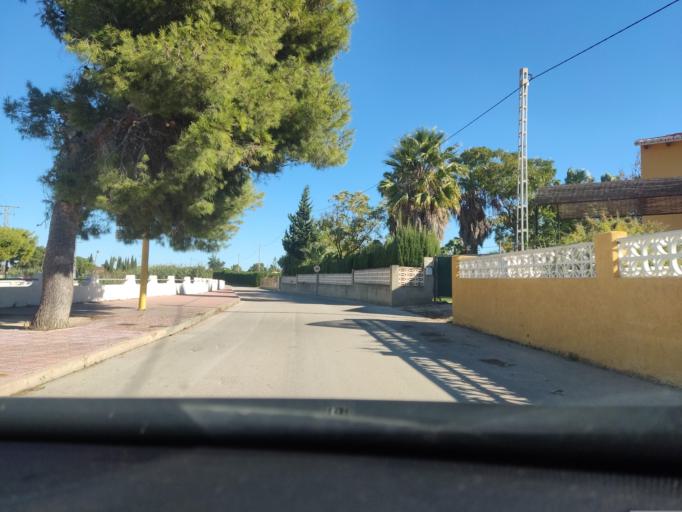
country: ES
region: Valencia
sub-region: Provincia de Alicante
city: els Poblets
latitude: 38.8501
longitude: 0.0207
